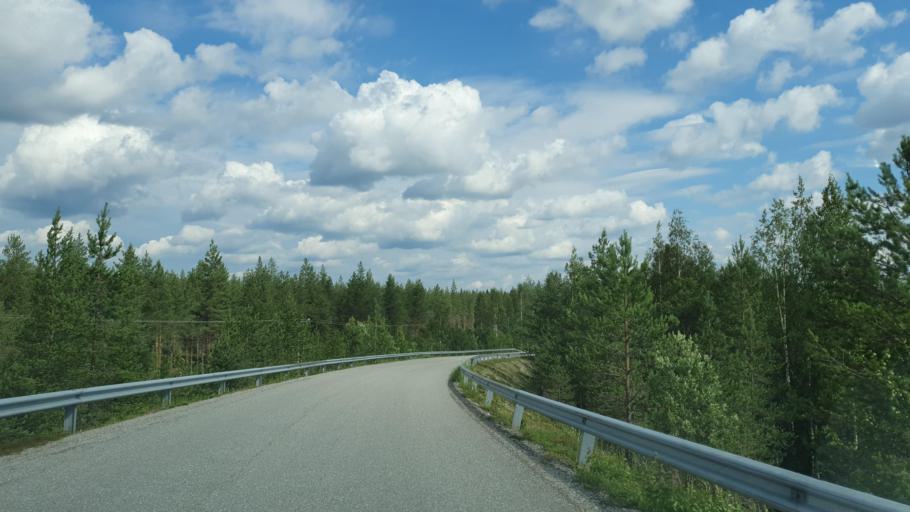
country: FI
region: Kainuu
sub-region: Kehys-Kainuu
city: Kuhmo
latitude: 64.4933
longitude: 29.5958
